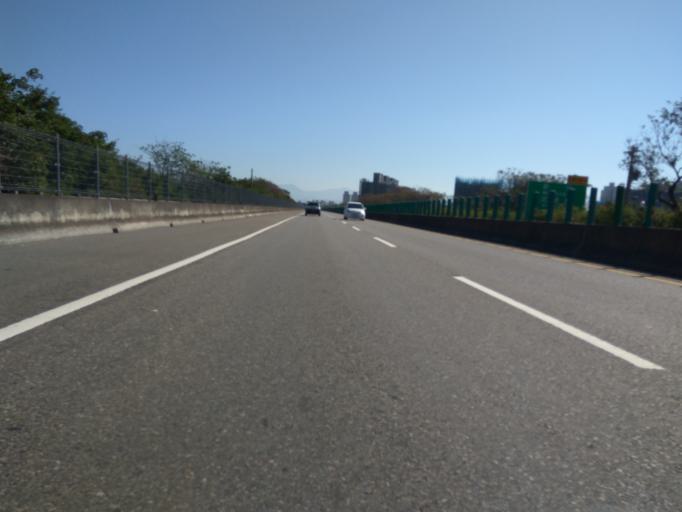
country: TW
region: Taiwan
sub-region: Hsinchu
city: Hsinchu
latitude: 24.8291
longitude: 120.9621
